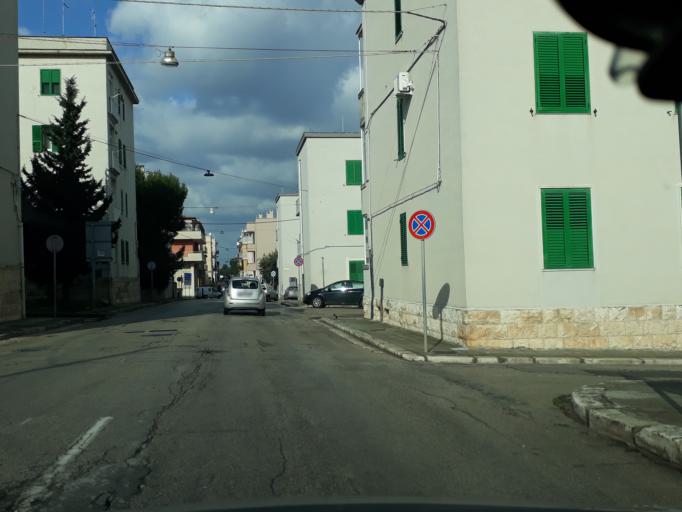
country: IT
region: Apulia
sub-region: Provincia di Brindisi
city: Fasano
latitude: 40.8307
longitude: 17.3554
